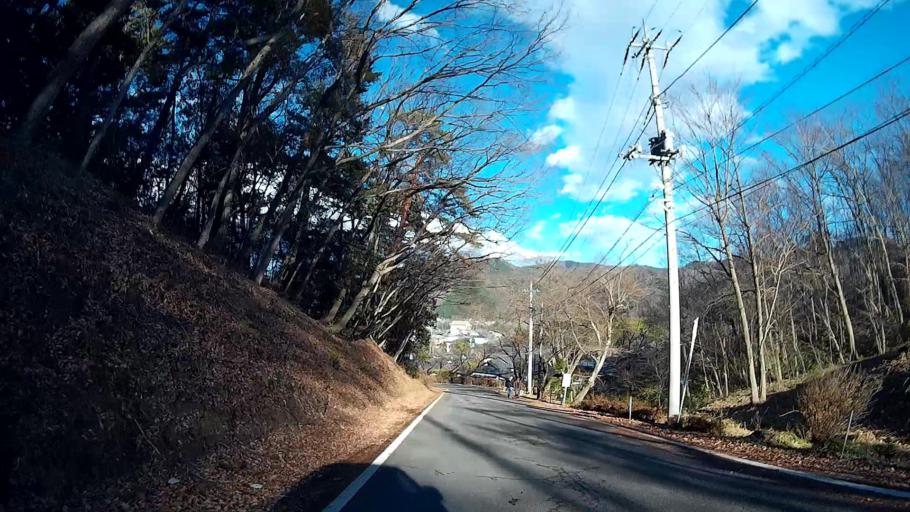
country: JP
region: Saitama
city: Yorii
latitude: 36.0916
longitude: 139.1041
